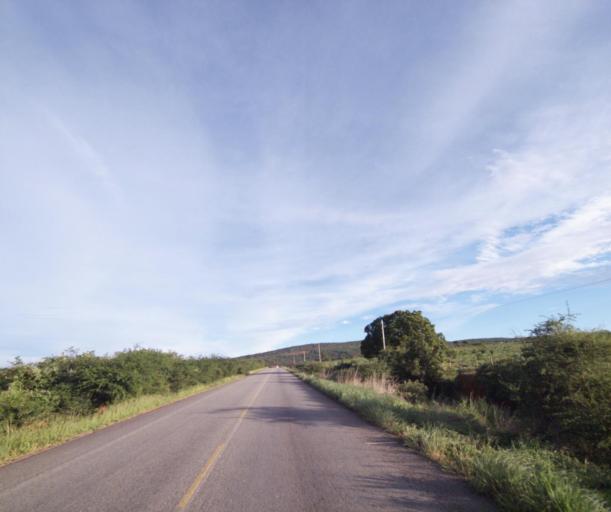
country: BR
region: Bahia
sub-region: Cacule
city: Cacule
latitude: -14.1856
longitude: -42.1624
